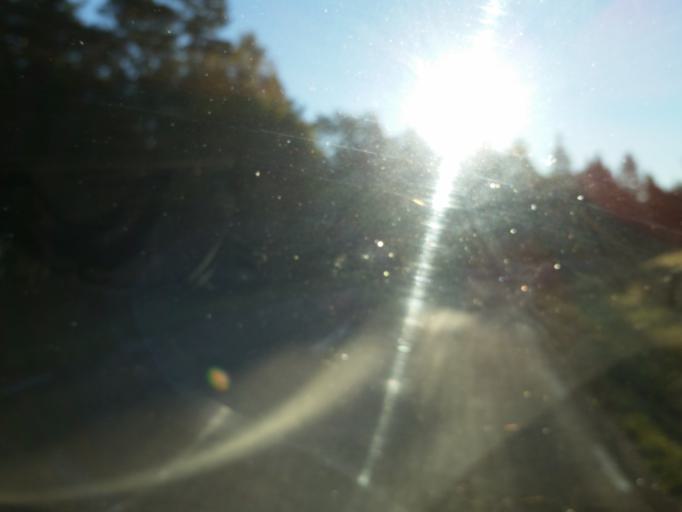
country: AX
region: Alands skaergard
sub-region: Vardoe
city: Vardoe
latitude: 60.2271
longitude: 20.4091
